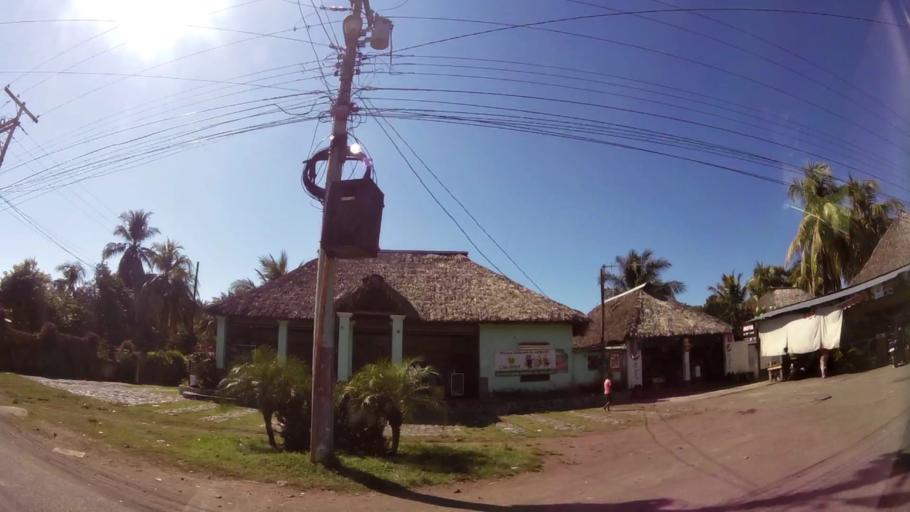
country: GT
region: Escuintla
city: Iztapa
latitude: 13.9172
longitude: -90.5518
